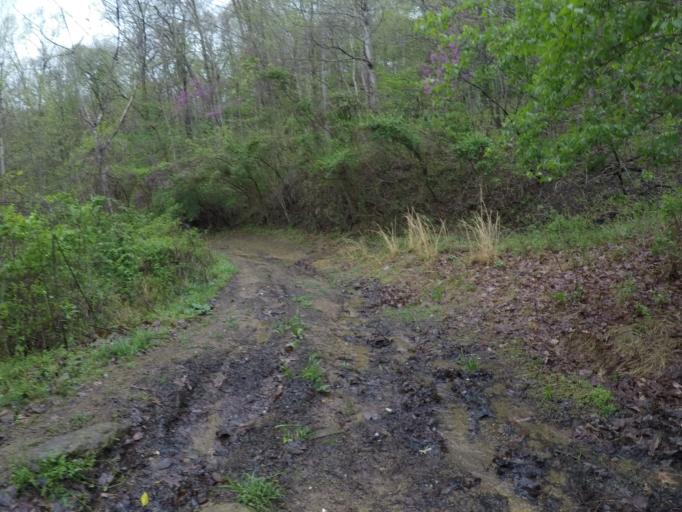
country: US
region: West Virginia
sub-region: Cabell County
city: Huntington
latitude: 38.3849
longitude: -82.4867
